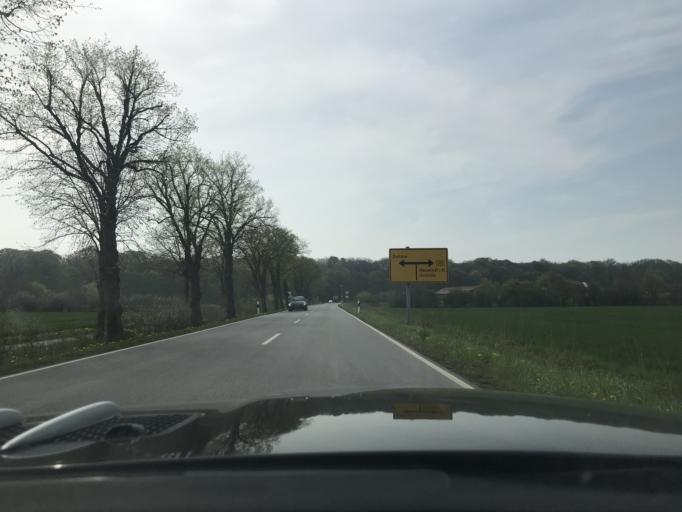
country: DE
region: Schleswig-Holstein
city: Grube
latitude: 54.2094
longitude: 11.0385
